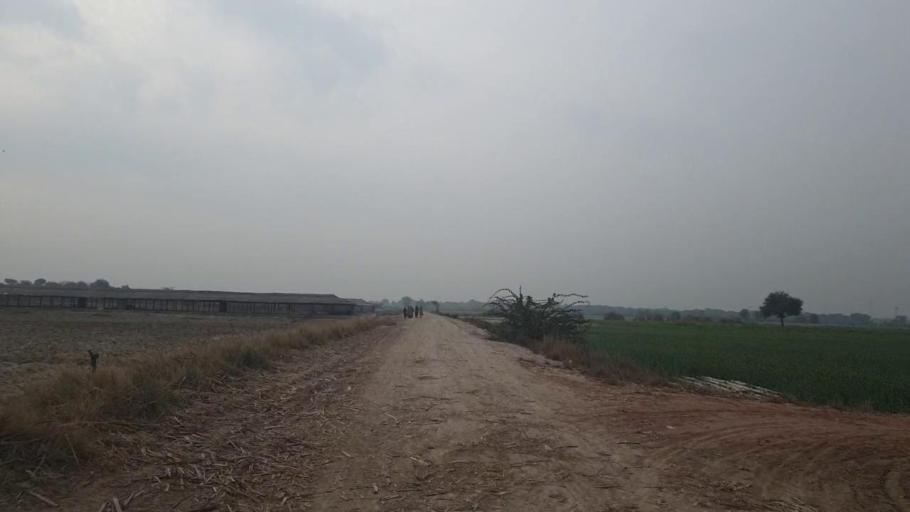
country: PK
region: Sindh
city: Tando Adam
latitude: 25.7355
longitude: 68.6824
